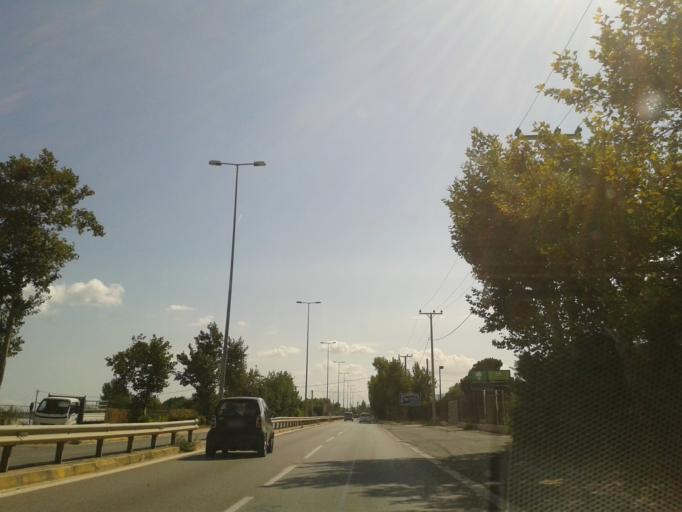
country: GR
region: Attica
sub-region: Nomarchia Anatolikis Attikis
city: Aghios Panteleimon
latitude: 38.1265
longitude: 23.9688
